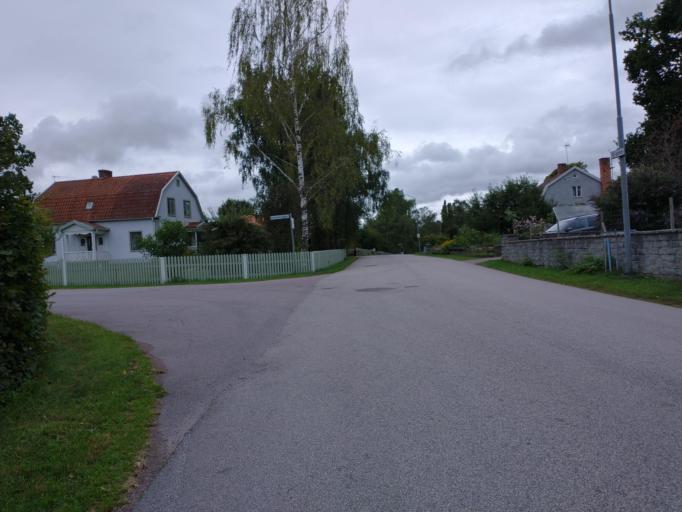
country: SE
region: Kalmar
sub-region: Kalmar Kommun
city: Lindsdal
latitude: 56.7854
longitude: 16.2936
